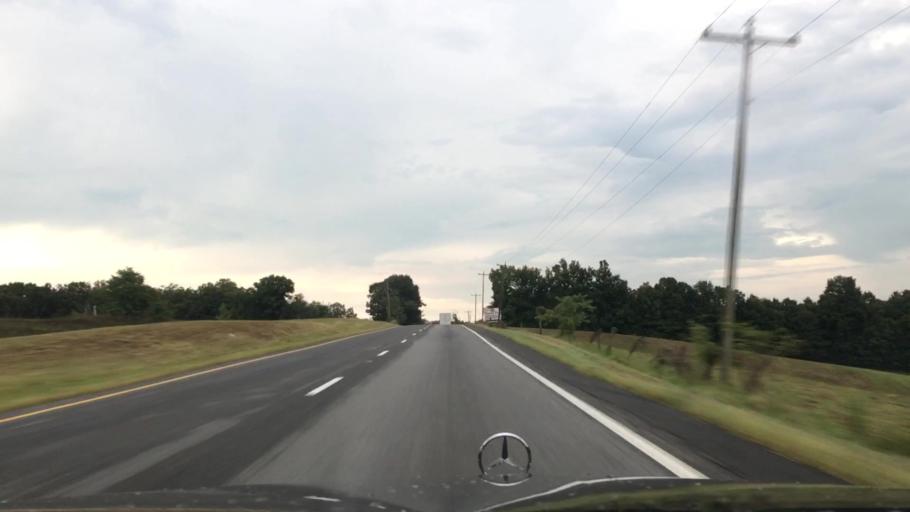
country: US
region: Virginia
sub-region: Frederick County
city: Shawnee Land
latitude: 39.3561
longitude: -78.3054
